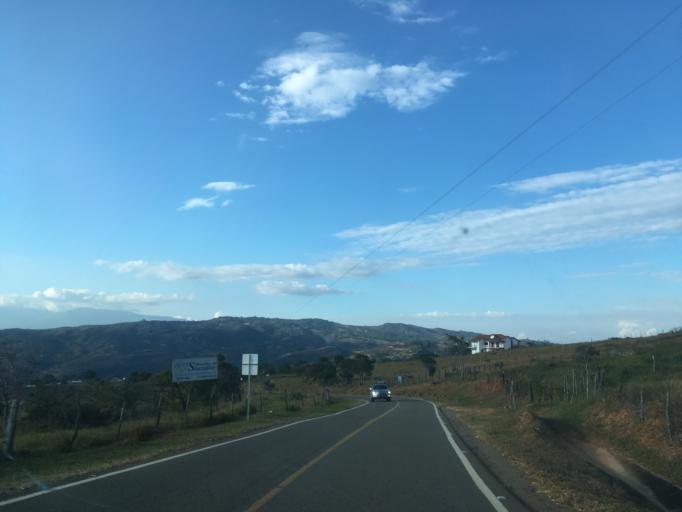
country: CO
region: Santander
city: Villanueva
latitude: 6.6326
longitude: -73.1797
